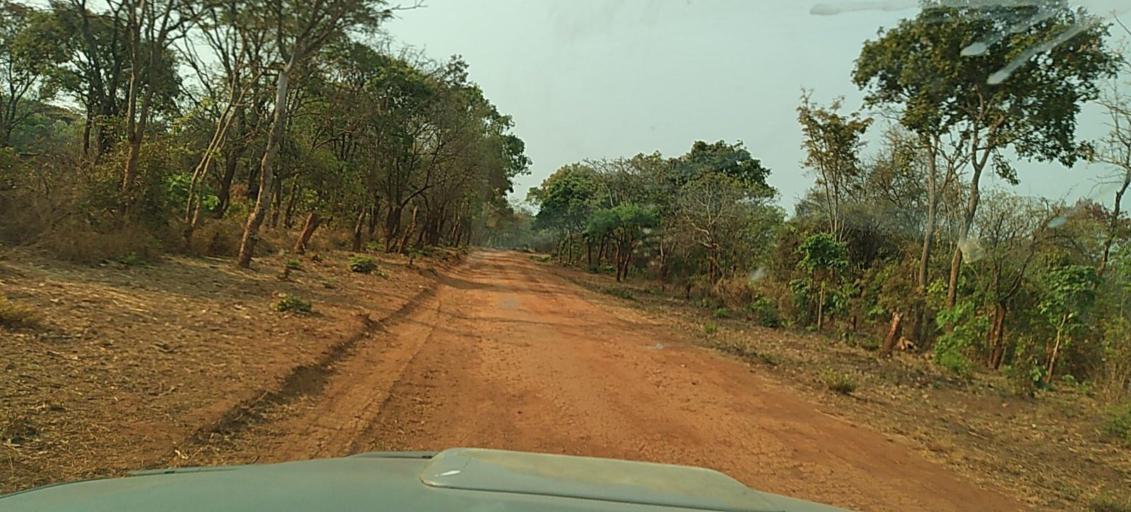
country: ZM
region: North-Western
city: Kasempa
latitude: -13.2947
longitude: 26.5545
